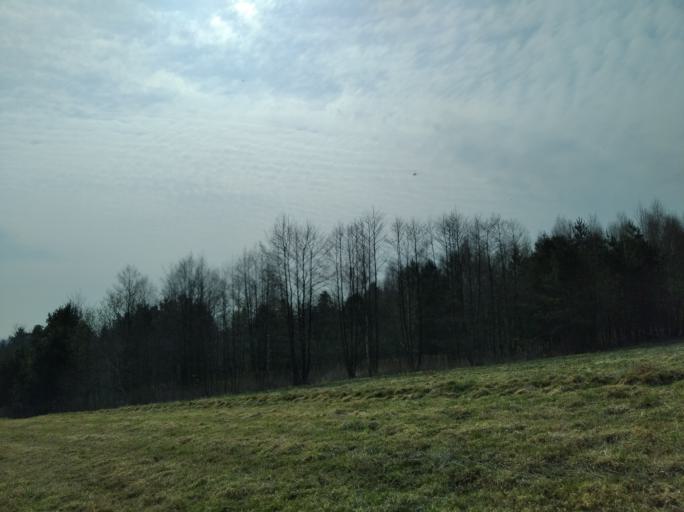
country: PL
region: Subcarpathian Voivodeship
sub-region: Powiat strzyzowski
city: Strzyzow
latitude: 49.8164
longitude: 21.8224
